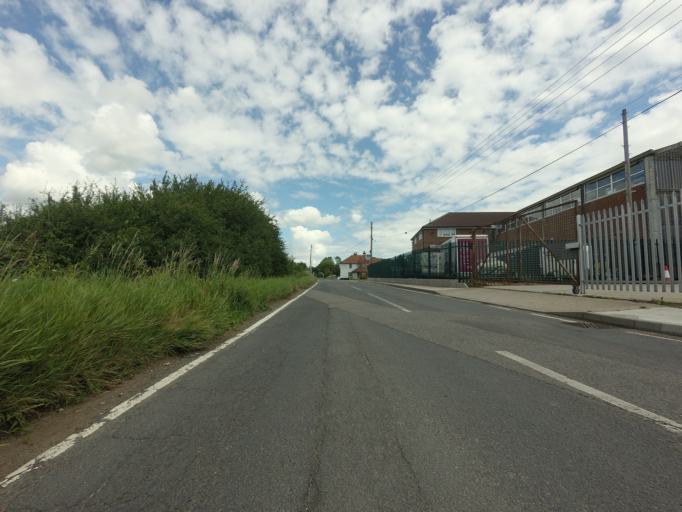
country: GB
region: England
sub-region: Medway
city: High Halstow
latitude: 51.4513
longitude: 0.5882
